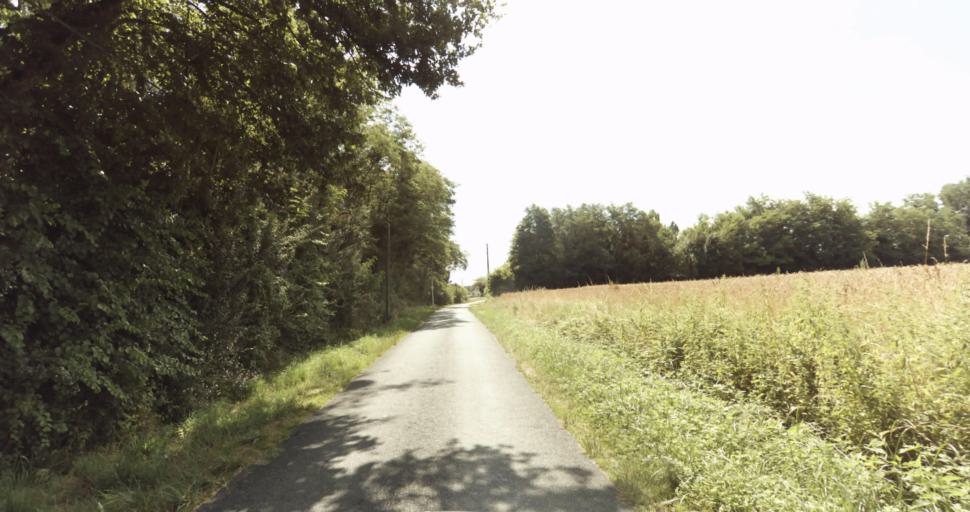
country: FR
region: Aquitaine
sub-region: Departement de la Gironde
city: Bazas
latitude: 44.4483
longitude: -0.2022
